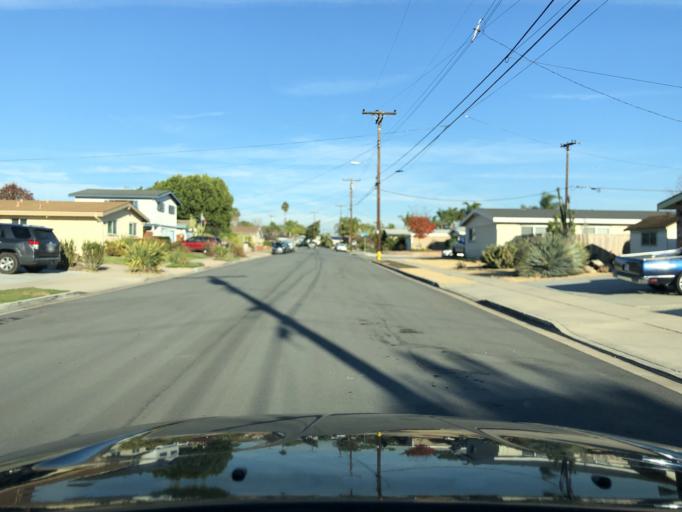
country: US
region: California
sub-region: San Diego County
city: La Jolla
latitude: 32.8186
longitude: -117.1978
